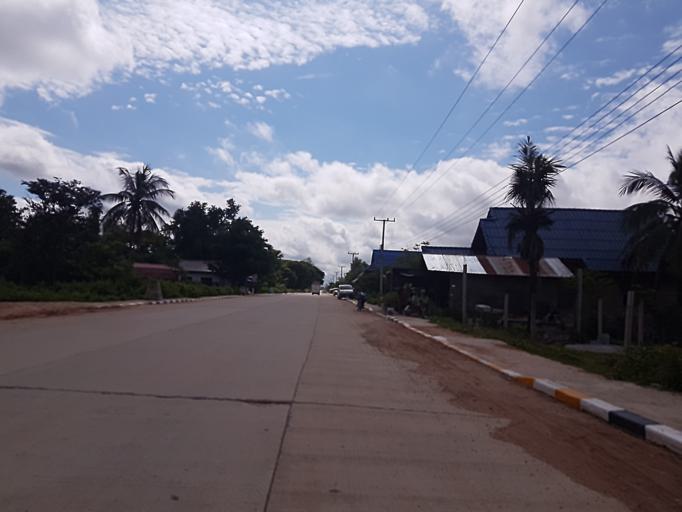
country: TH
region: Nong Khai
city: Nong Khai
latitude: 17.9167
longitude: 102.6899
